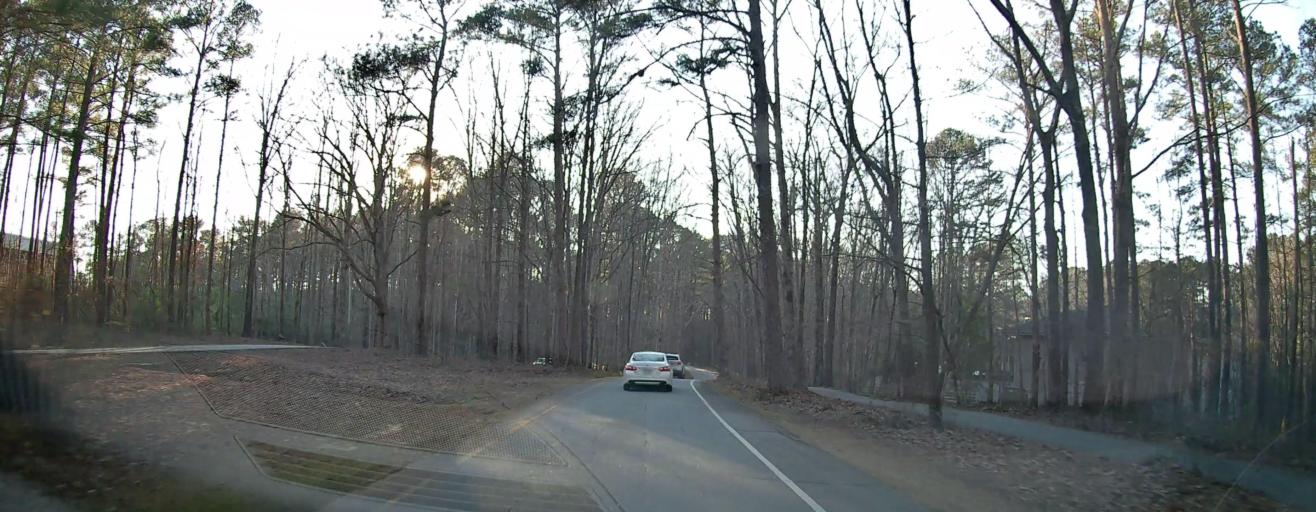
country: US
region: Georgia
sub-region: Fayette County
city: Peachtree City
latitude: 33.4043
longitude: -84.5924
